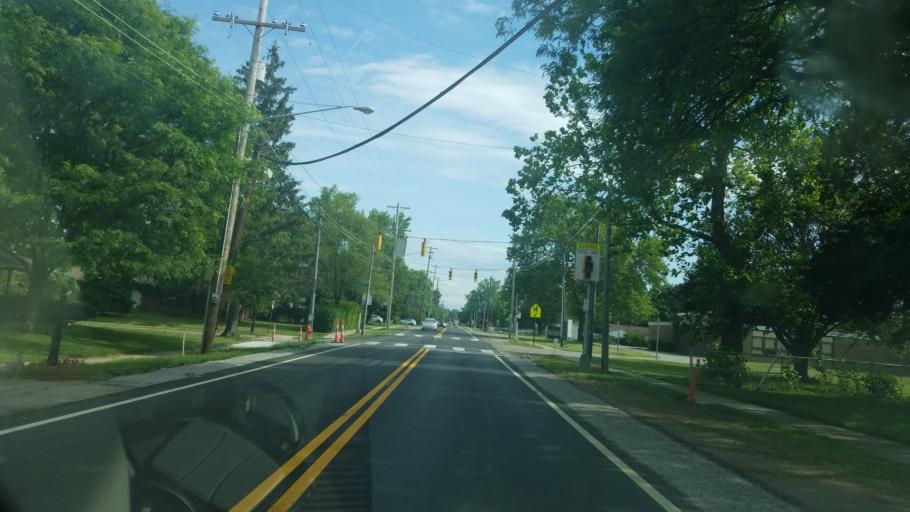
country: US
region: Ohio
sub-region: Franklin County
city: Worthington
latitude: 40.0540
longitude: -82.9879
